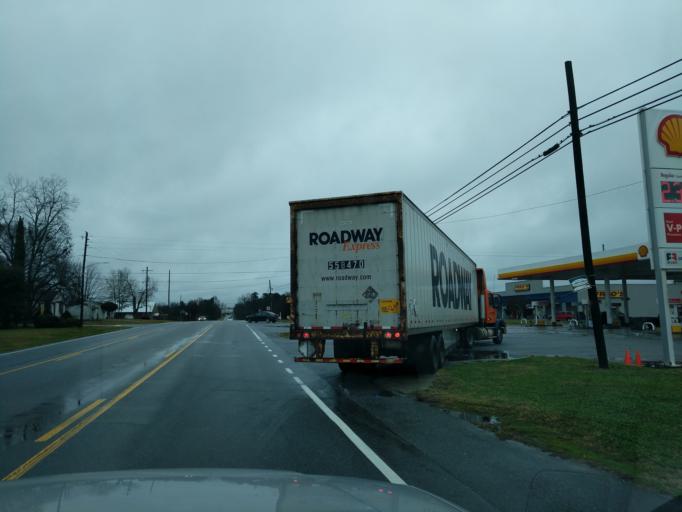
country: US
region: Georgia
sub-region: Franklin County
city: Lavonia
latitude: 34.4236
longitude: -83.1036
